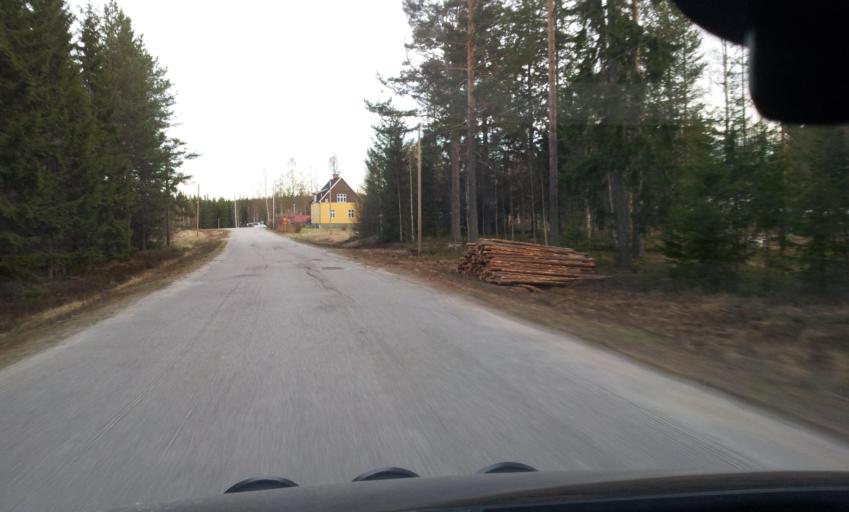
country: SE
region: Gaevleborg
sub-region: Ljusdals Kommun
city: Farila
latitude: 62.0033
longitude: 15.8380
